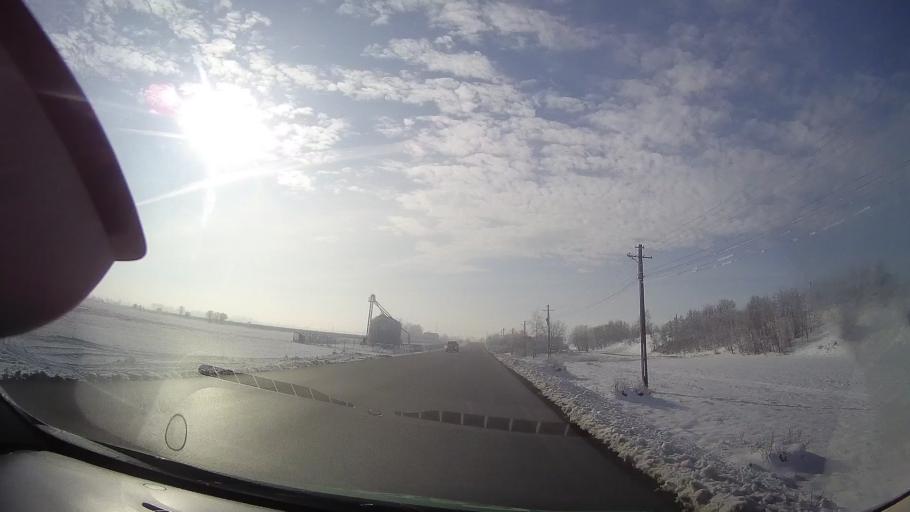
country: RO
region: Neamt
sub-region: Comuna Timisesti
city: Timisesti
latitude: 47.2529
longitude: 26.5518
